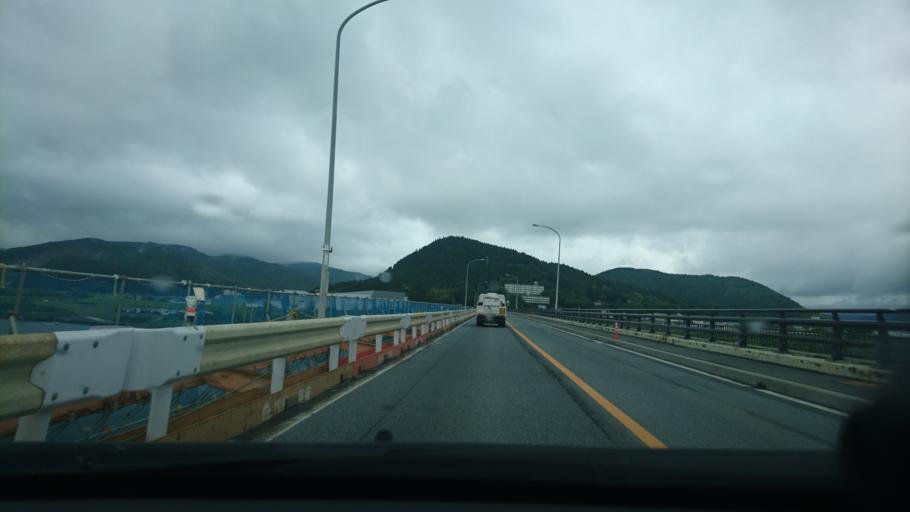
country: JP
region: Miyagi
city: Ishinomaki
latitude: 38.5134
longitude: 141.3071
